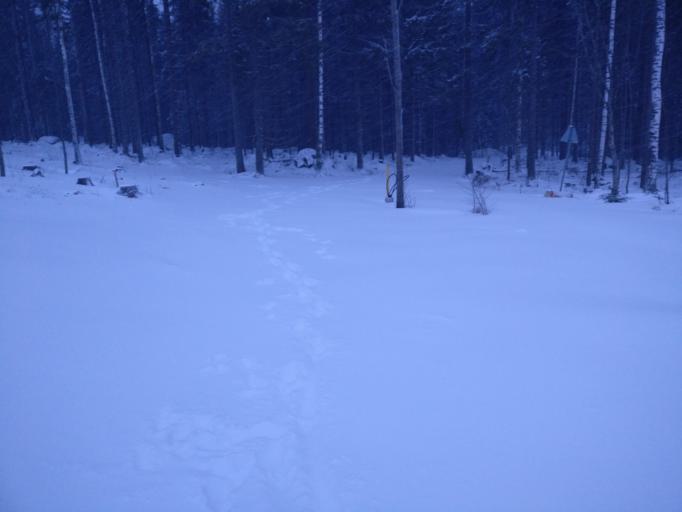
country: FI
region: Pirkanmaa
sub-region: Tampere
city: Tampere
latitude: 61.4422
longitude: 23.8144
